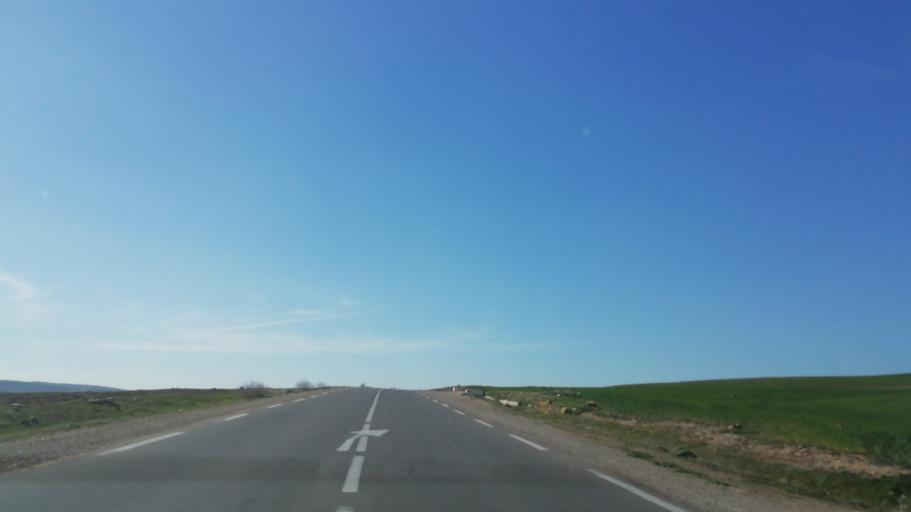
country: DZ
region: Mascara
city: Oued el Abtal
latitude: 35.4474
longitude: 0.8157
